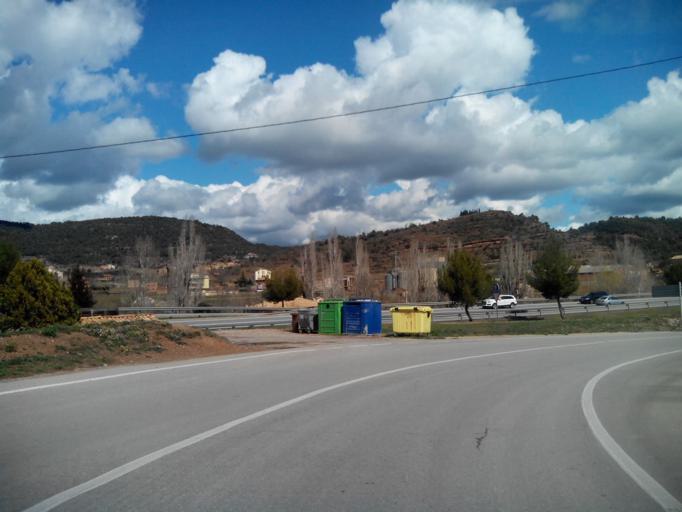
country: ES
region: Catalonia
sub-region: Provincia de Barcelona
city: Cardona
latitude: 41.9185
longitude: 1.6805
